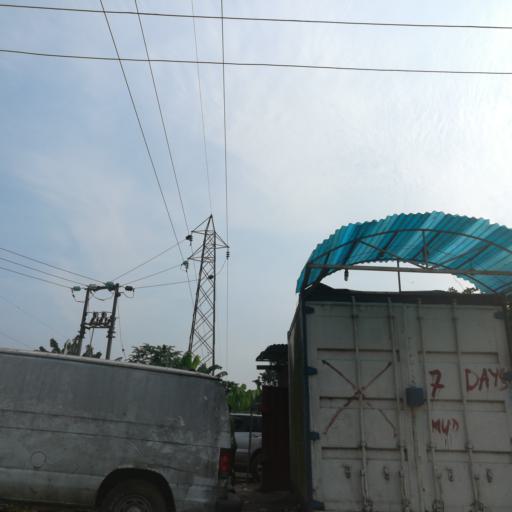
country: NG
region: Rivers
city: Port Harcourt
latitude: 4.8446
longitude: 7.0480
